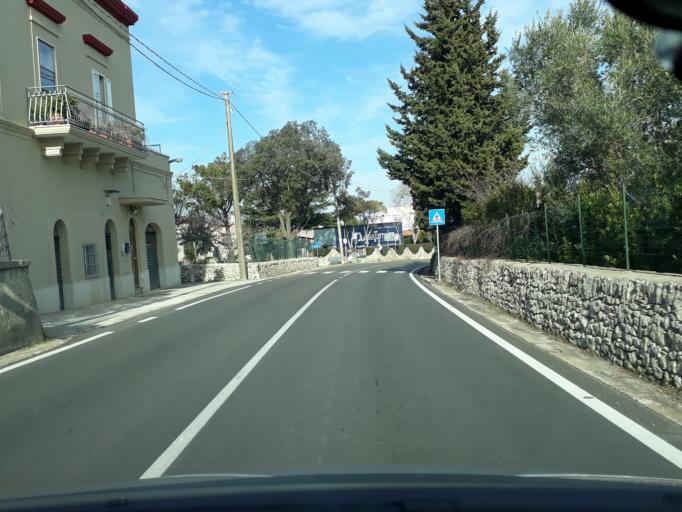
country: IT
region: Apulia
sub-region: Provincia di Brindisi
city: Lamie di Olimpie-Selva
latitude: 40.7959
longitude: 17.3490
